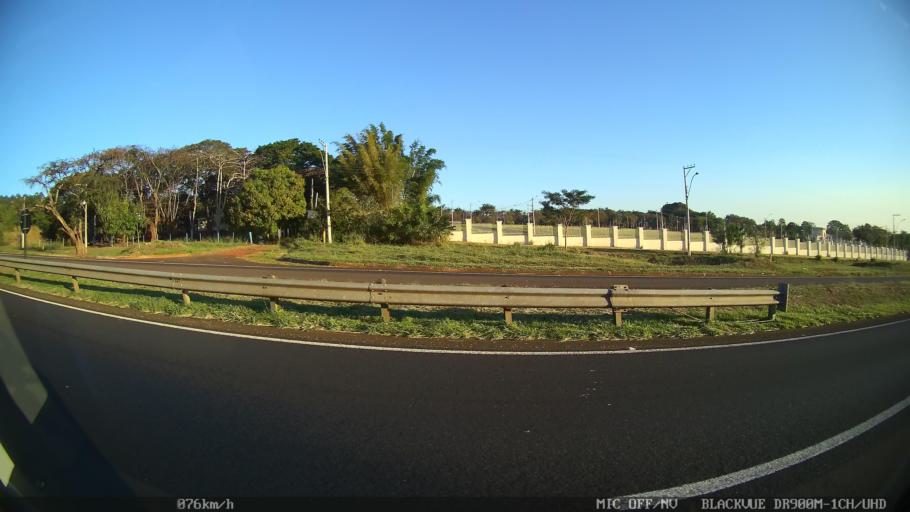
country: BR
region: Sao Paulo
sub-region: Araraquara
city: Araraquara
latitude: -21.8178
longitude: -48.1842
